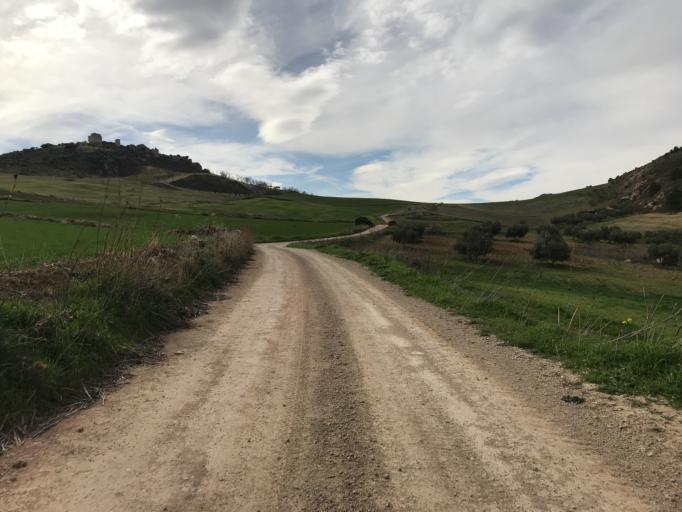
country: ES
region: Andalusia
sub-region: Provincia de Malaga
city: Ardales
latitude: 36.8771
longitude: -4.8768
